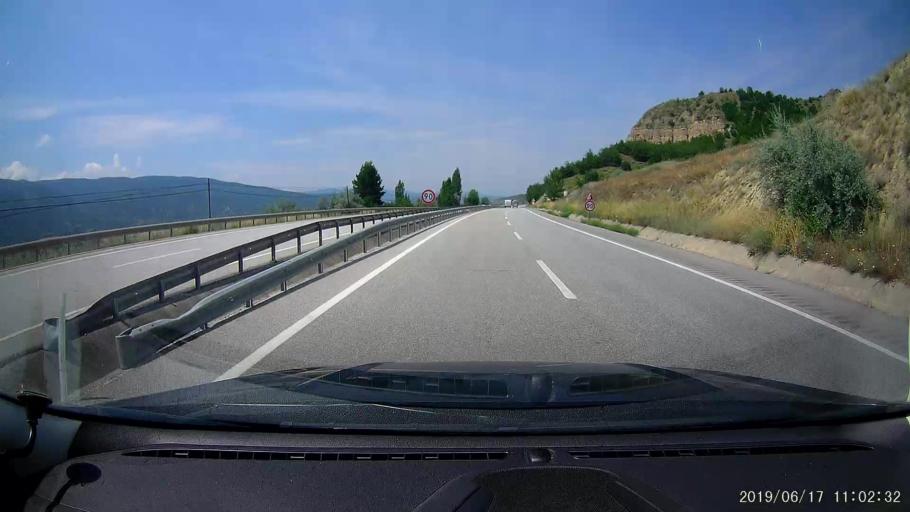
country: TR
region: Kastamonu
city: Tosya
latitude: 41.0171
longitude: 34.1344
